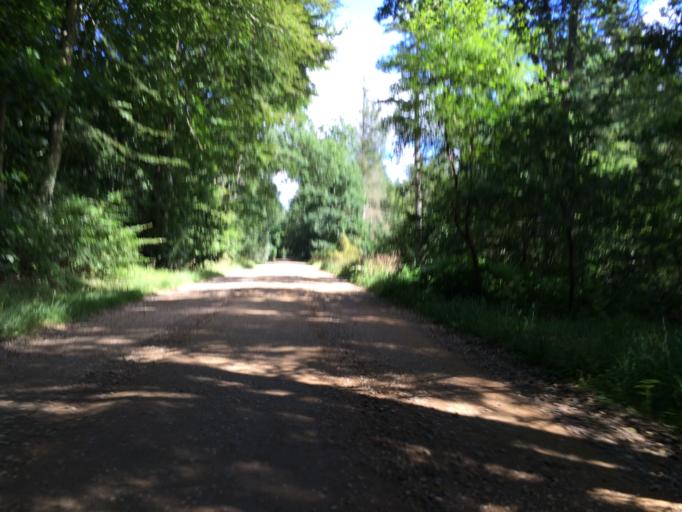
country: DK
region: Central Jutland
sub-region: Holstebro Kommune
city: Ulfborg
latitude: 56.2841
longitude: 8.1669
